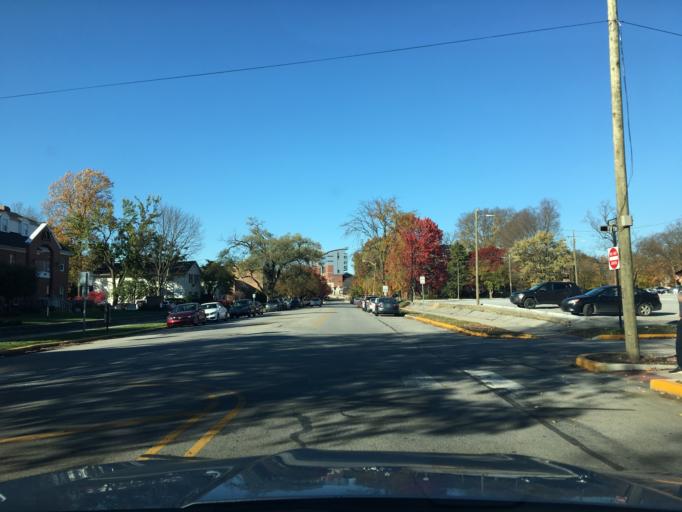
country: US
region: Indiana
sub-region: Tippecanoe County
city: West Lafayette
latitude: 40.4291
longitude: -86.9191
